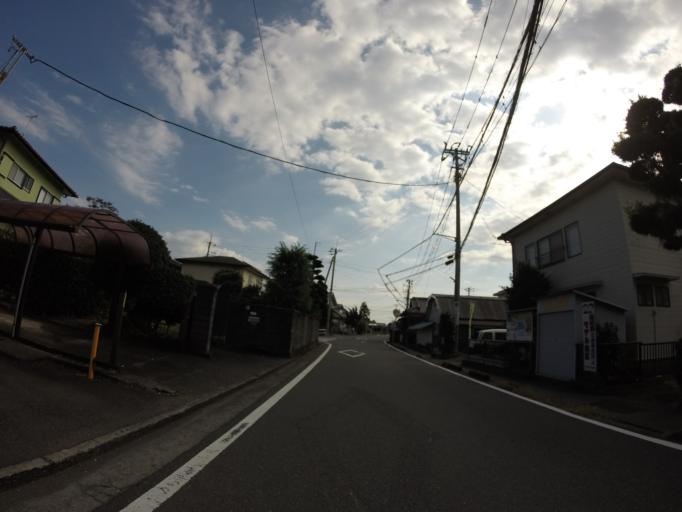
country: JP
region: Shizuoka
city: Fuji
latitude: 35.1637
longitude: 138.6324
